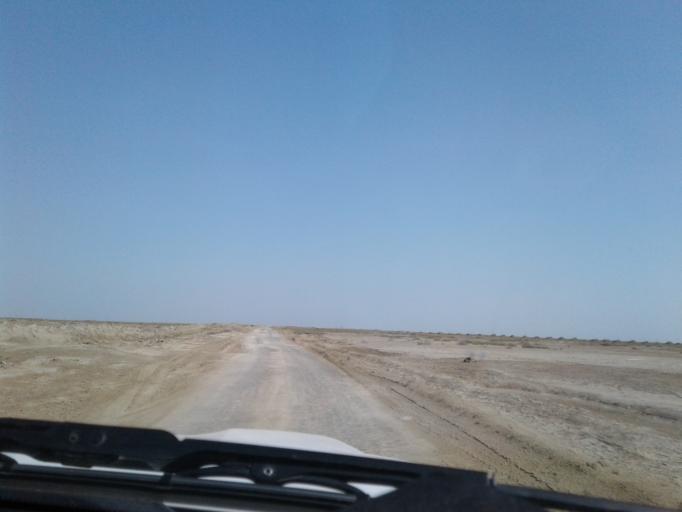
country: IR
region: Golestan
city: Gomishan
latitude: 37.8243
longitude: 53.9215
